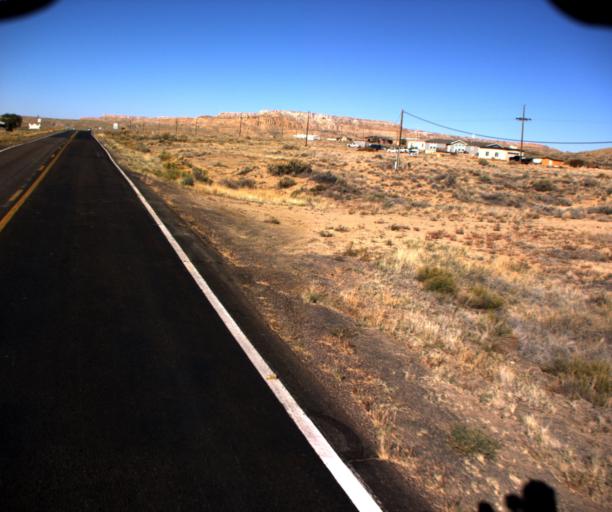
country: US
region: Arizona
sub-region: Navajo County
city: First Mesa
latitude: 35.7926
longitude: -110.4919
